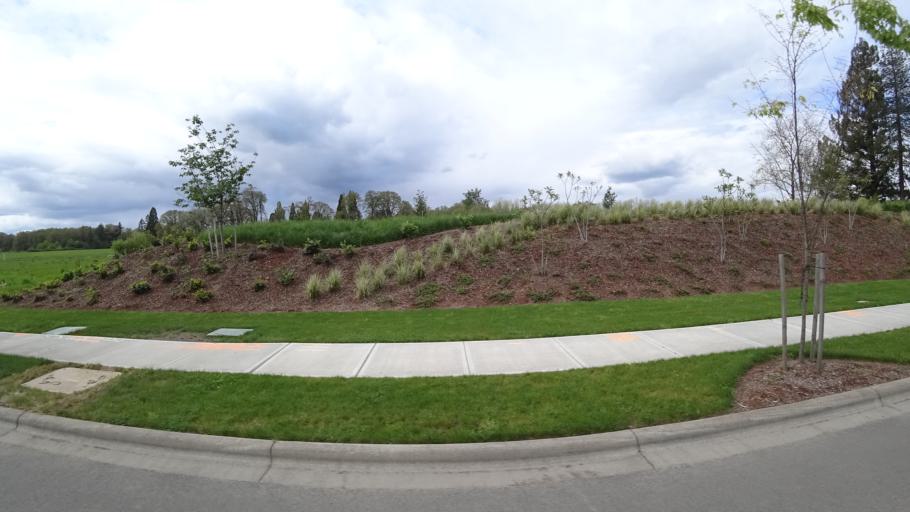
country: US
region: Oregon
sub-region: Washington County
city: Hillsboro
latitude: 45.5513
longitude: -122.9510
